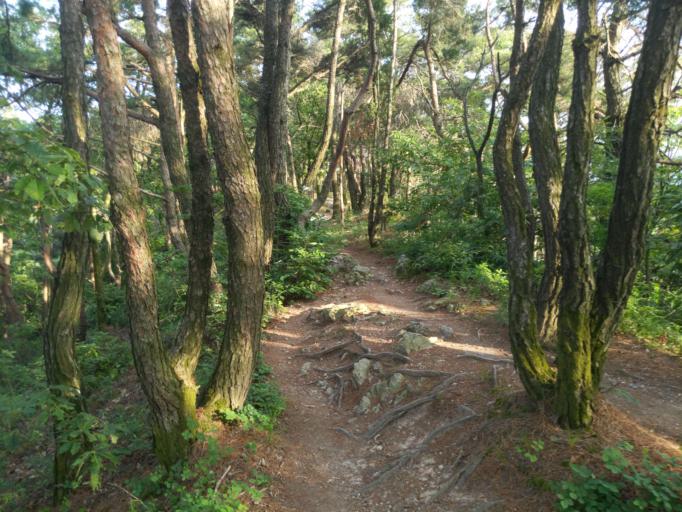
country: KR
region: Daegu
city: Hwawon
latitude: 35.7838
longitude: 128.5463
